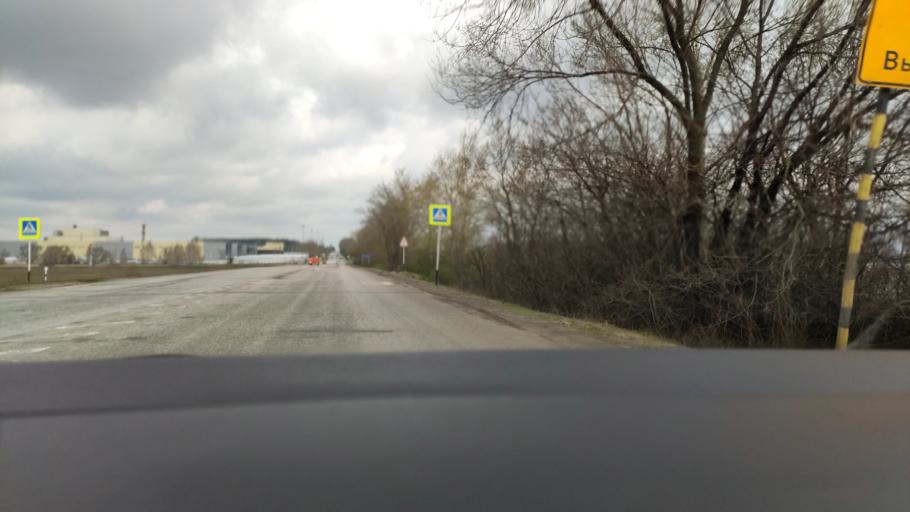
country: RU
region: Voronezj
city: Maslovka
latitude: 51.5476
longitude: 39.2834
